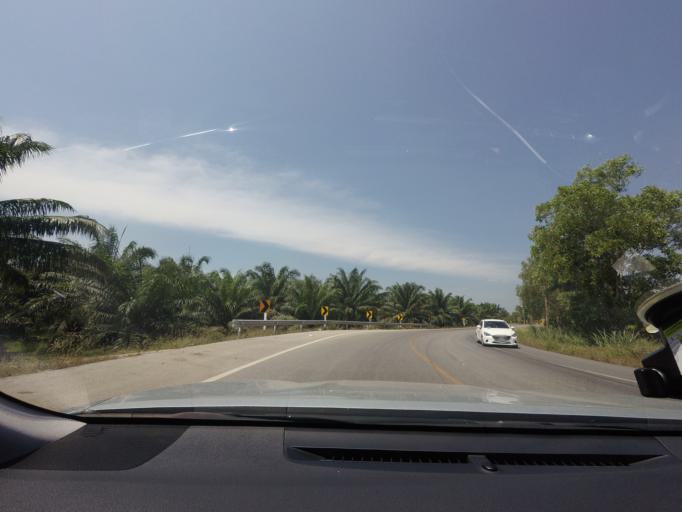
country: TH
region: Surat Thani
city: Tha Chang
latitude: 9.2128
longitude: 99.1977
